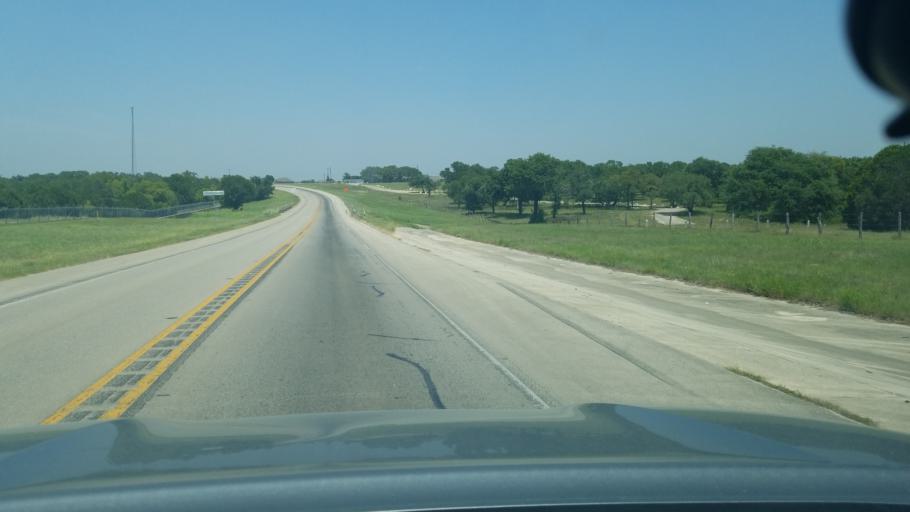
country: US
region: Texas
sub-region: Bexar County
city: Timberwood Park
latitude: 29.7096
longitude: -98.5170
